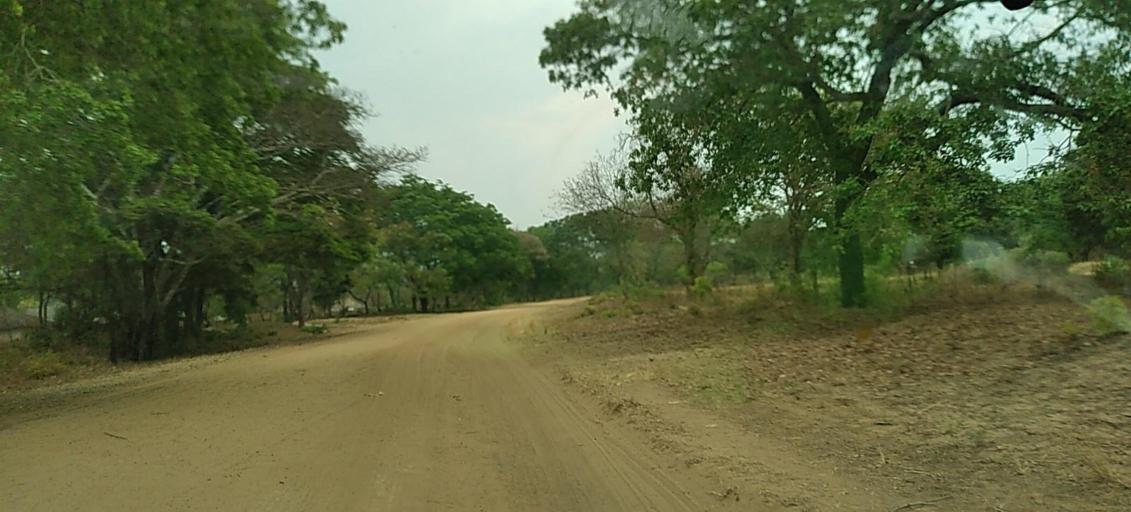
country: ZM
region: North-Western
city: Kabompo
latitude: -13.3743
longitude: 24.2984
